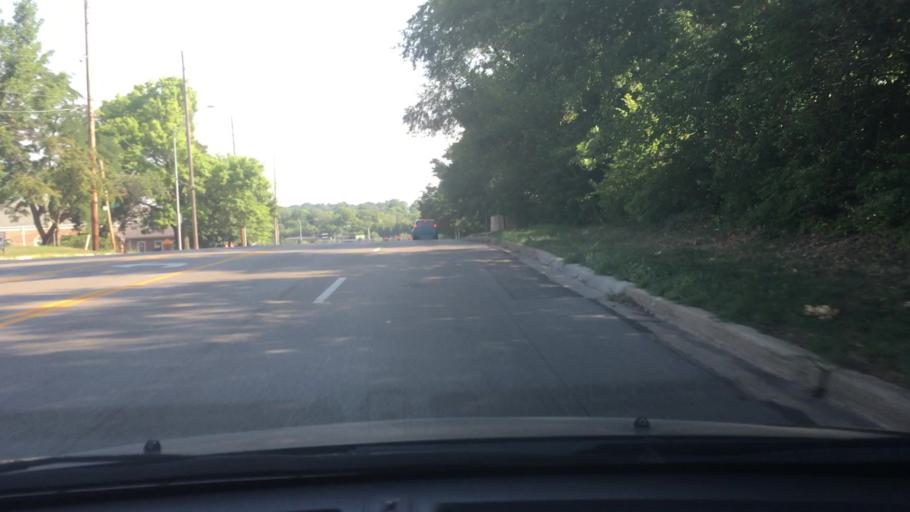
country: US
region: Kansas
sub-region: Johnson County
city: Leawood
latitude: 38.9538
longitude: -94.5958
